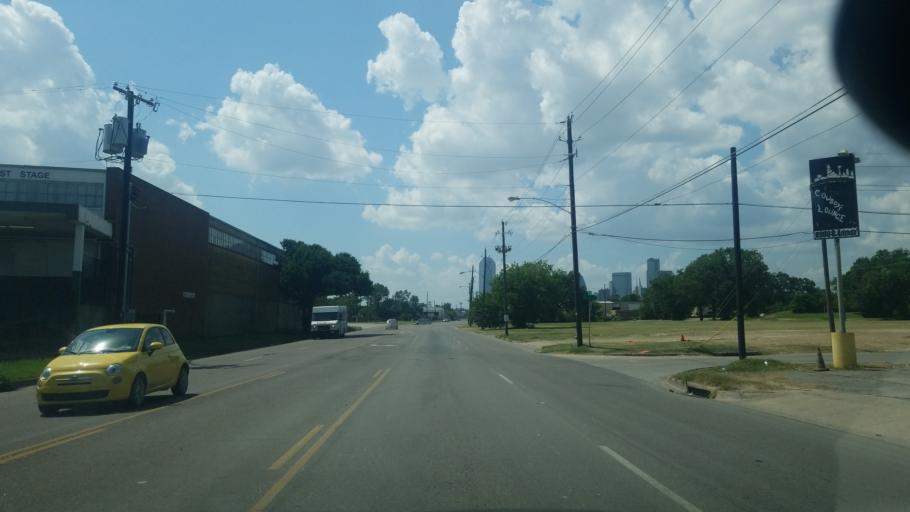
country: US
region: Texas
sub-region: Dallas County
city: Dallas
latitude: 32.7589
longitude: -96.7820
